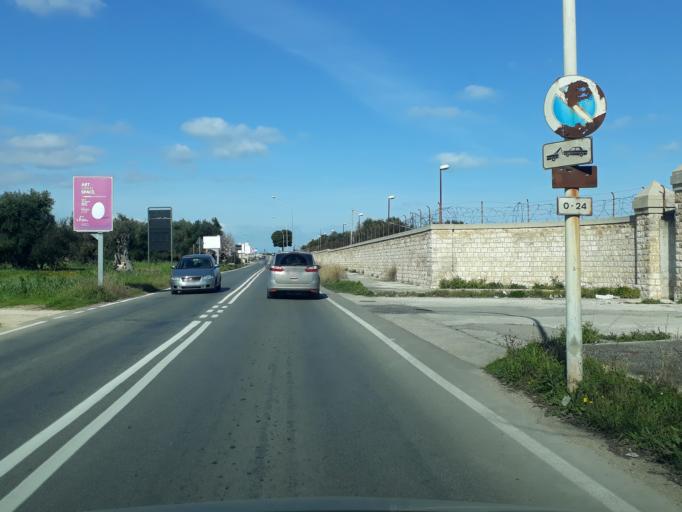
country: IT
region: Apulia
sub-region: Provincia di Bari
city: Monopoli
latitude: 40.9526
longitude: 17.2855
